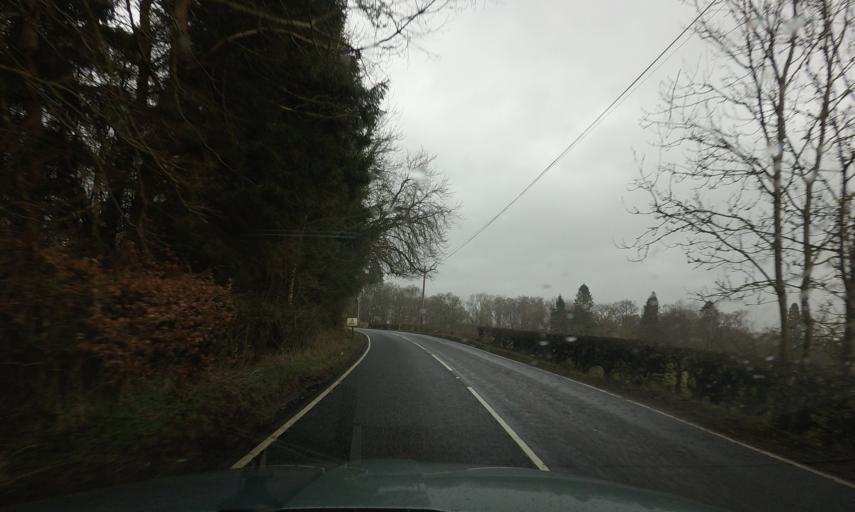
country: GB
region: Scotland
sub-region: Stirling
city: Balfron
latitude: 56.0968
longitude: -4.3608
